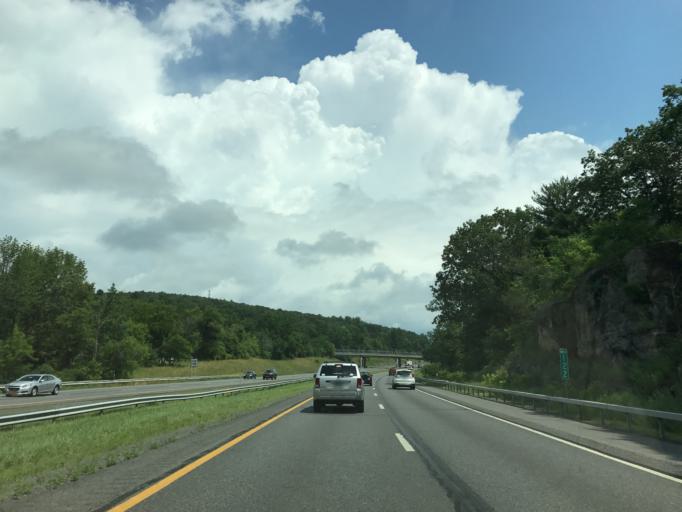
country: US
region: New York
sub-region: Greene County
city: Coxsackie
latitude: 42.3626
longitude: -73.8479
